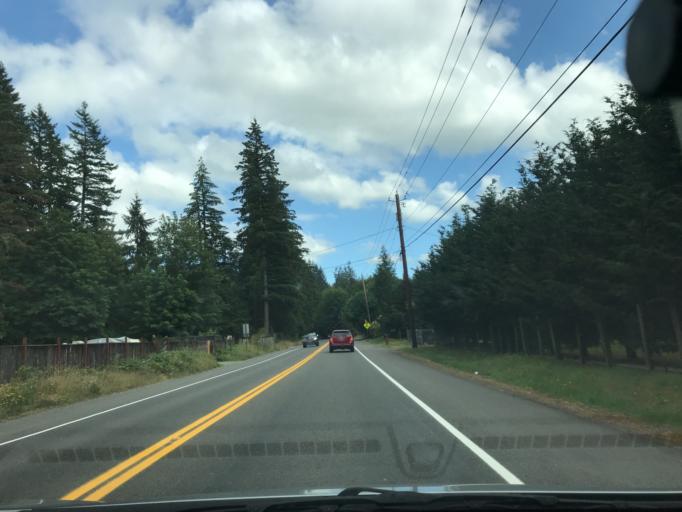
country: US
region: Washington
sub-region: King County
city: Lake Morton-Berrydale
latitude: 47.2993
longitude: -122.0844
